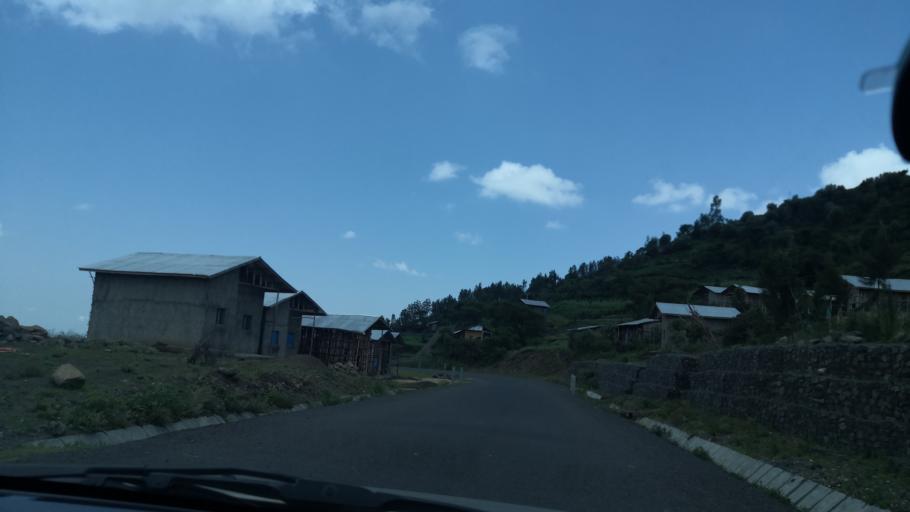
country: ET
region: Amhara
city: Abomsa
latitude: 10.3148
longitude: 39.8743
